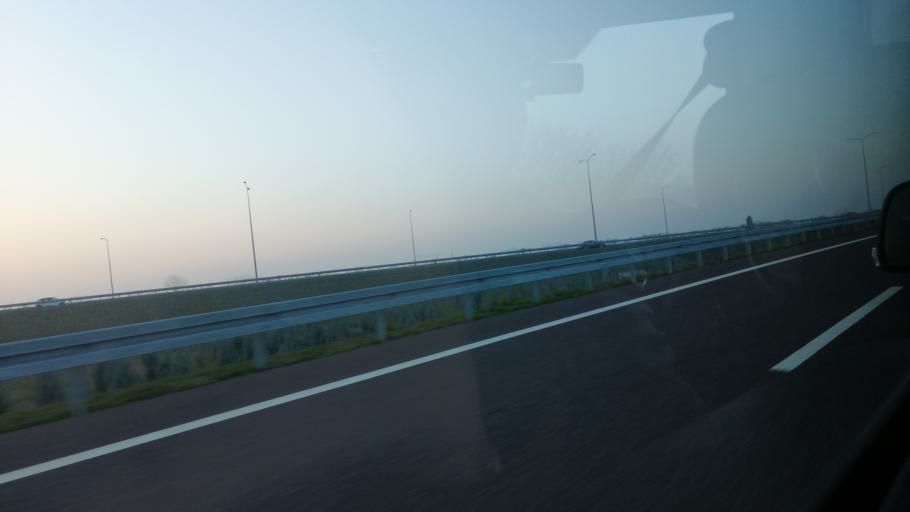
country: TR
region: Yalova
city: Altinova
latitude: 40.6993
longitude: 29.4895
